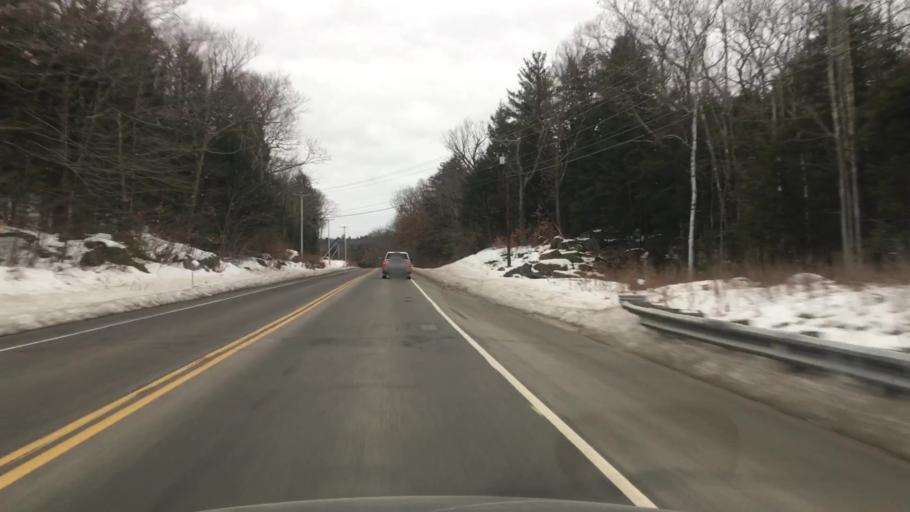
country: US
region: New Hampshire
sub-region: Merrimack County
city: Newbury
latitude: 43.3054
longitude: -72.0123
